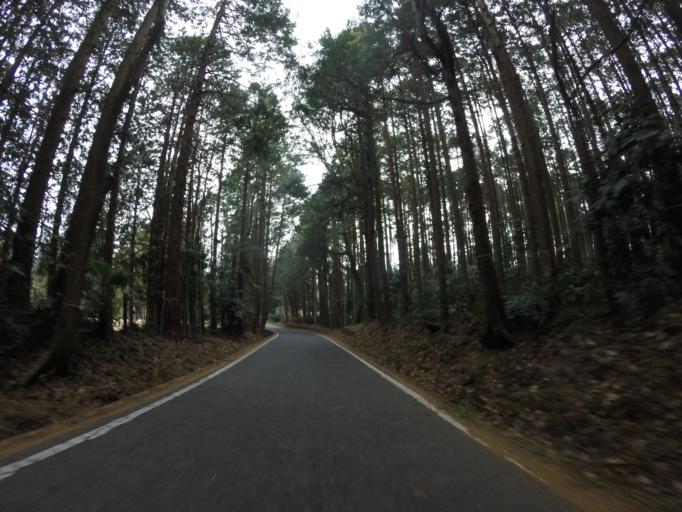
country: JP
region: Shizuoka
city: Fujinomiya
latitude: 35.2351
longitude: 138.5800
